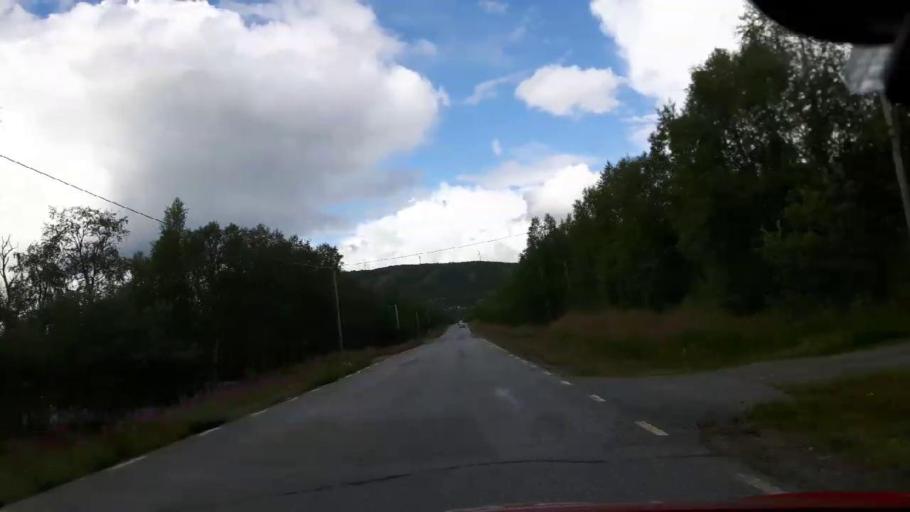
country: NO
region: Nordland
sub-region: Hattfjelldal
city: Hattfjelldal
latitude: 65.0644
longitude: 14.8348
